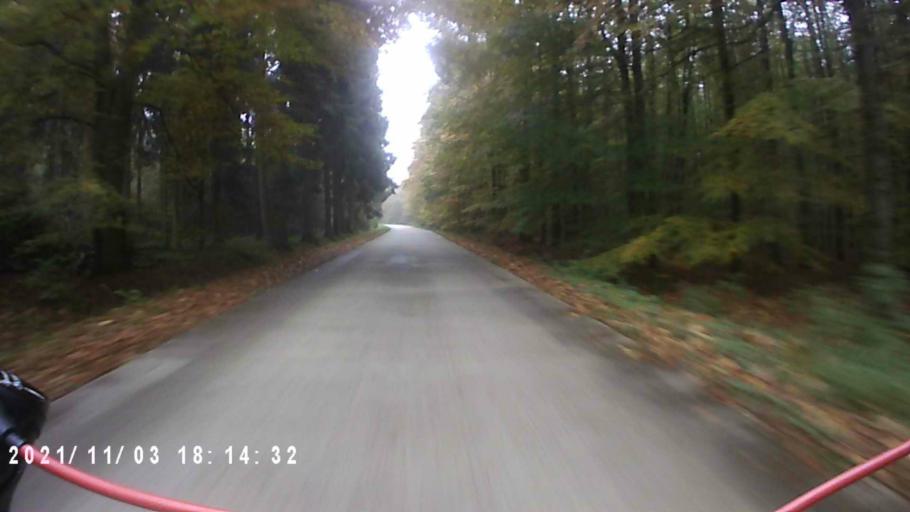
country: NL
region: Drenthe
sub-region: Gemeente Westerveld
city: Dwingeloo
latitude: 52.8162
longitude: 6.3951
